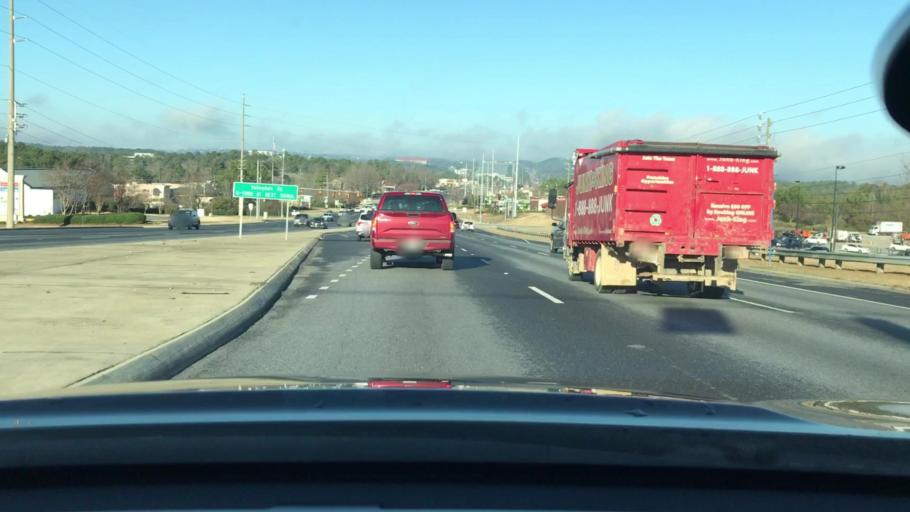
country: US
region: Alabama
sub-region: Shelby County
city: Lake Purdy
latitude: 33.4204
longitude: -86.6950
